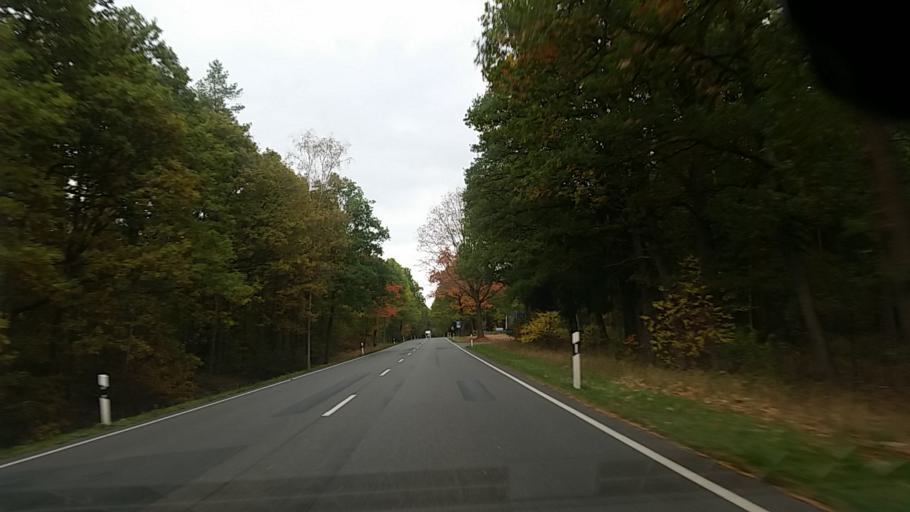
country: DE
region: Lower Saxony
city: Sprakensehl
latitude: 52.8056
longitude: 10.4877
